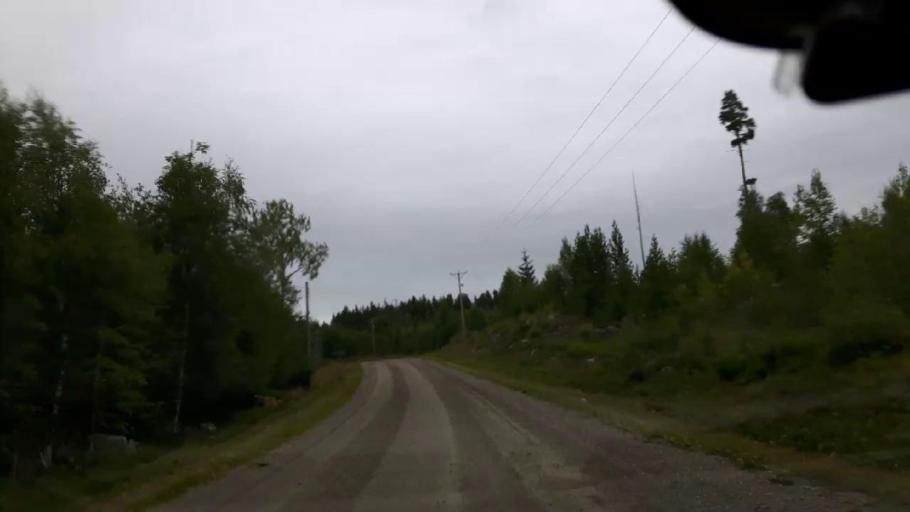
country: SE
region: Vaesternorrland
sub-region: Ange Kommun
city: Fransta
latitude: 62.7926
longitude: 16.0384
